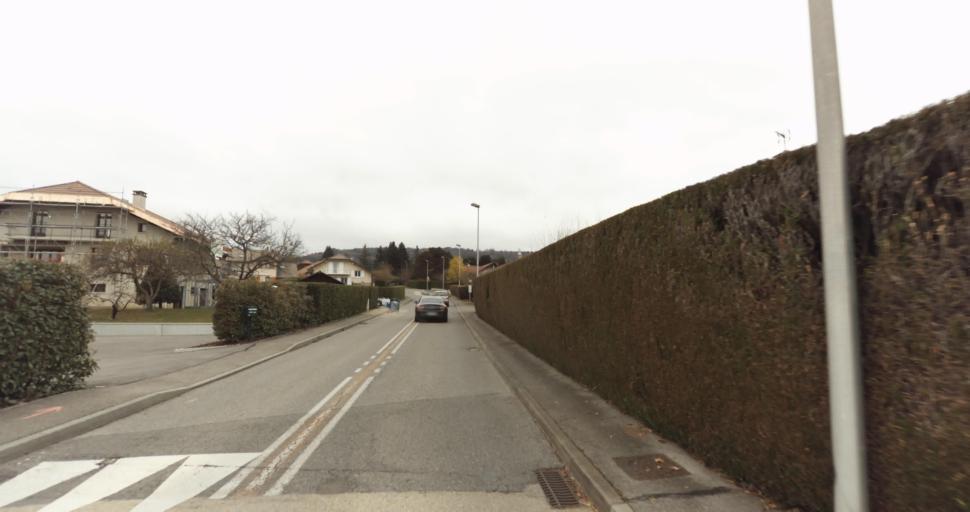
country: FR
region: Rhone-Alpes
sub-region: Departement de la Haute-Savoie
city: Metz-Tessy
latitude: 45.9447
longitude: 6.1085
